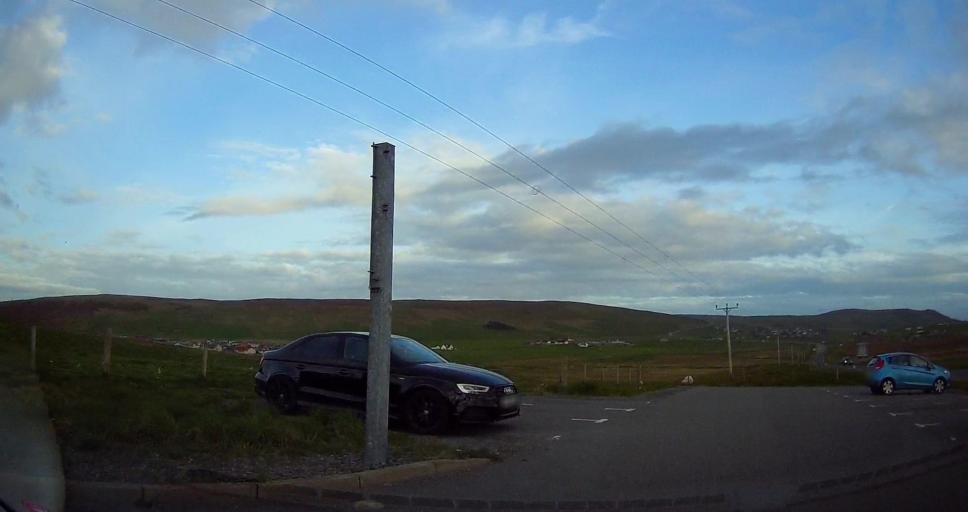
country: GB
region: Scotland
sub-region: Shetland Islands
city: Lerwick
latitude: 60.1987
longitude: -1.2320
